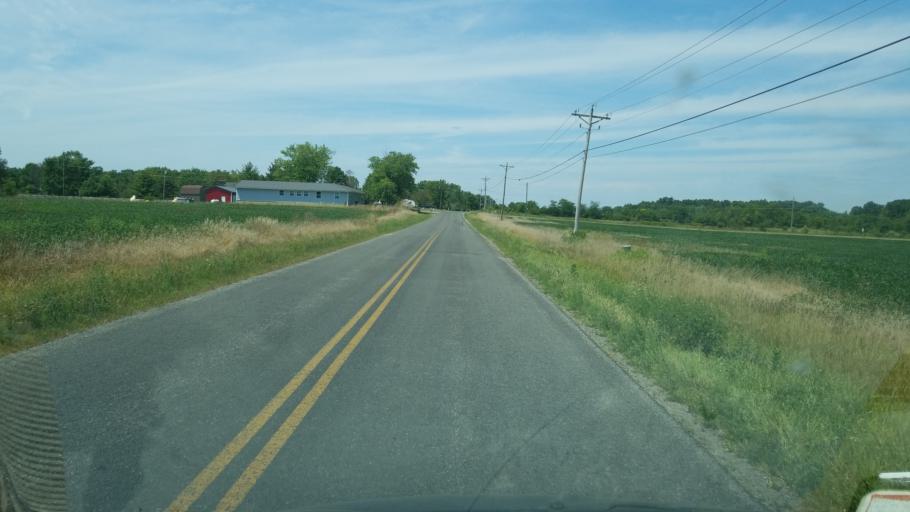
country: US
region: Ohio
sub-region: Union County
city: New California
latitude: 40.1532
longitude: -83.2616
